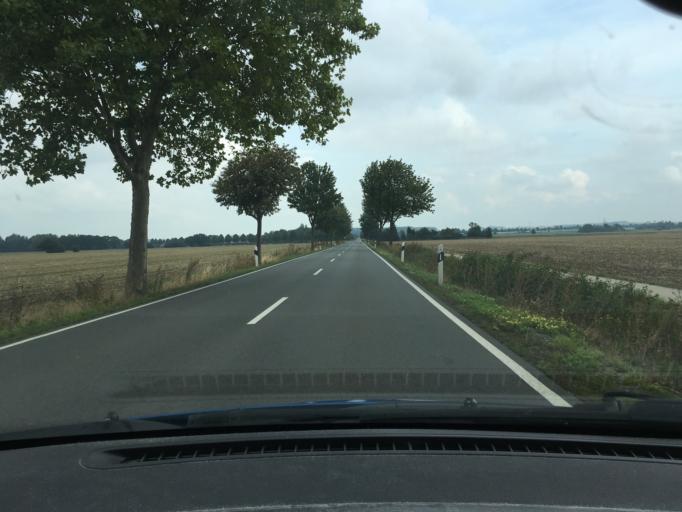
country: DE
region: Lower Saxony
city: Barsinghausen
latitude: 52.3236
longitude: 9.4677
